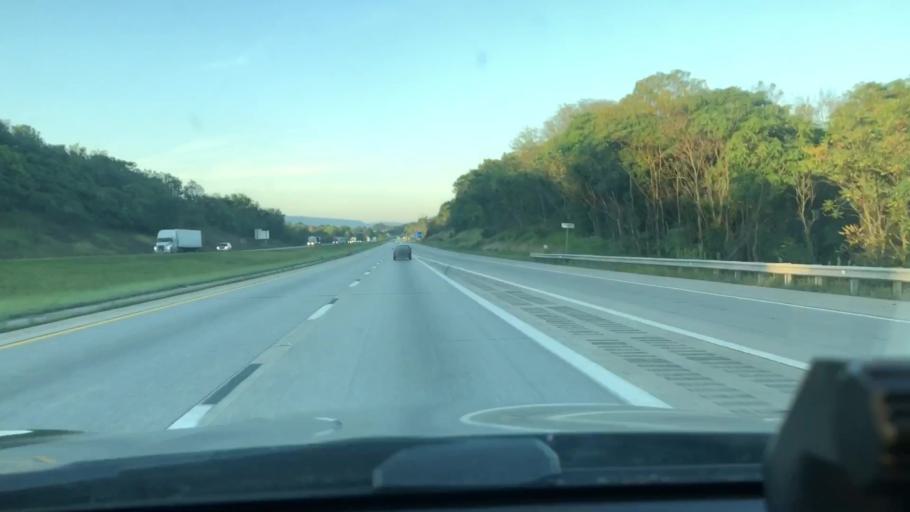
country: US
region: Pennsylvania
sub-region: Dauphin County
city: Skyline View
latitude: 40.3557
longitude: -76.7182
